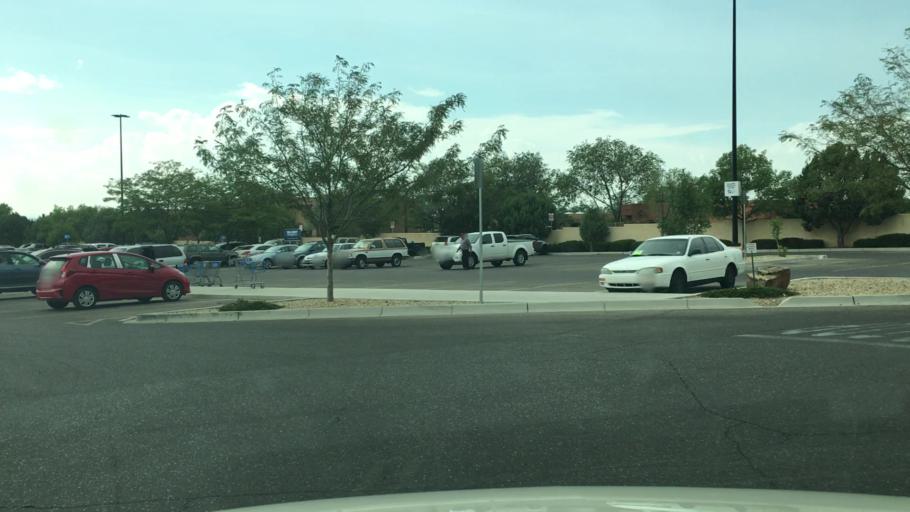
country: US
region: New Mexico
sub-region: Santa Fe County
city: Agua Fria
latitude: 35.6526
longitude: -105.9976
